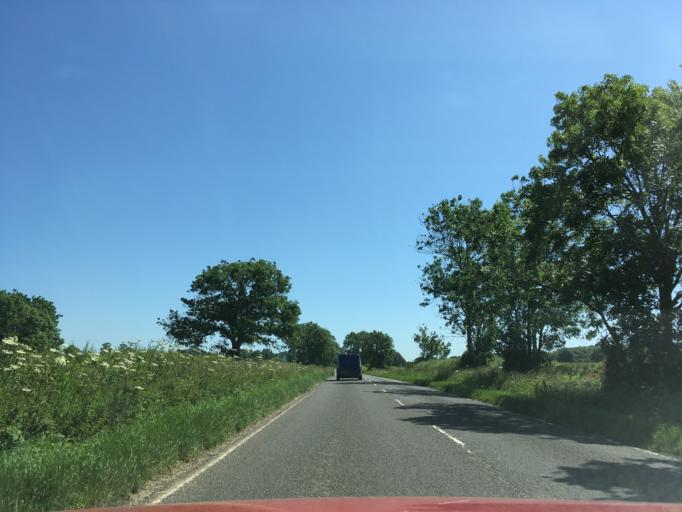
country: GB
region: England
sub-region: Northamptonshire
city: Brackley
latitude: 51.9961
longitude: -1.1702
